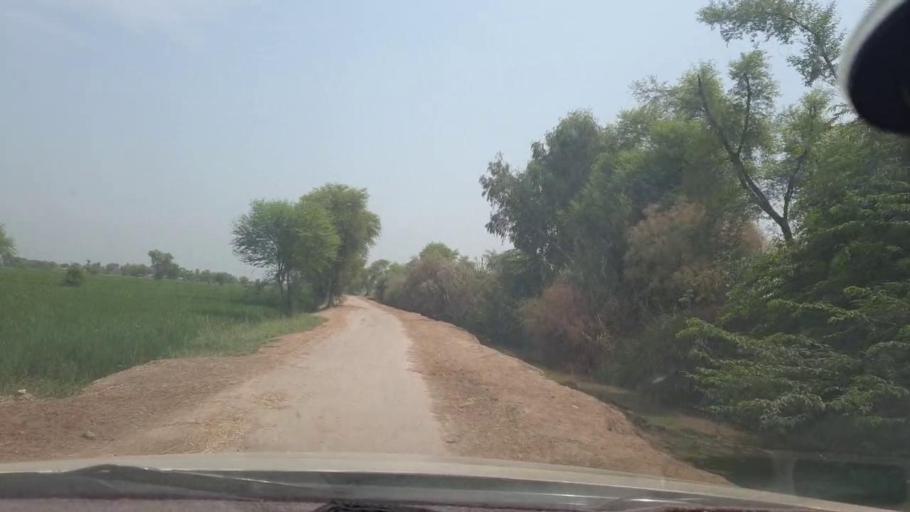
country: PK
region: Sindh
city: Jacobabad
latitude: 28.1775
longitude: 68.3829
